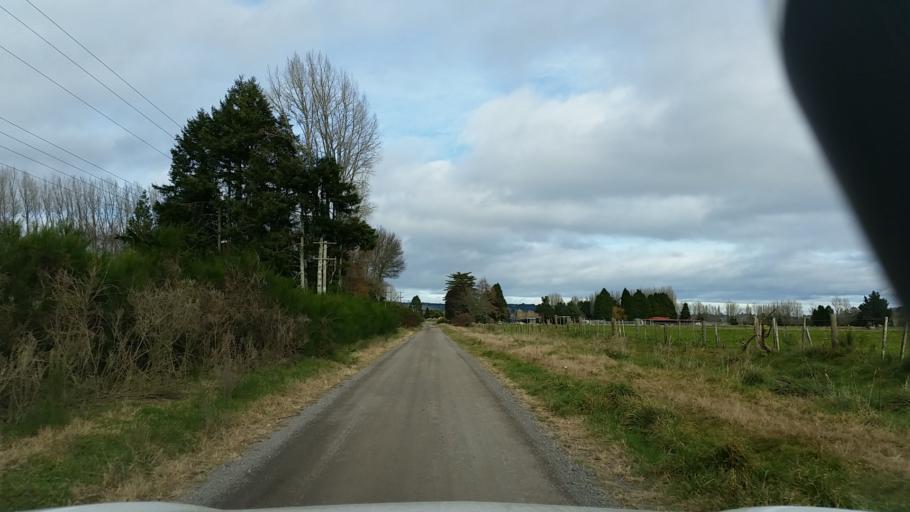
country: NZ
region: Bay of Plenty
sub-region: Kawerau District
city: Kawerau
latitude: -38.2817
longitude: 176.5525
